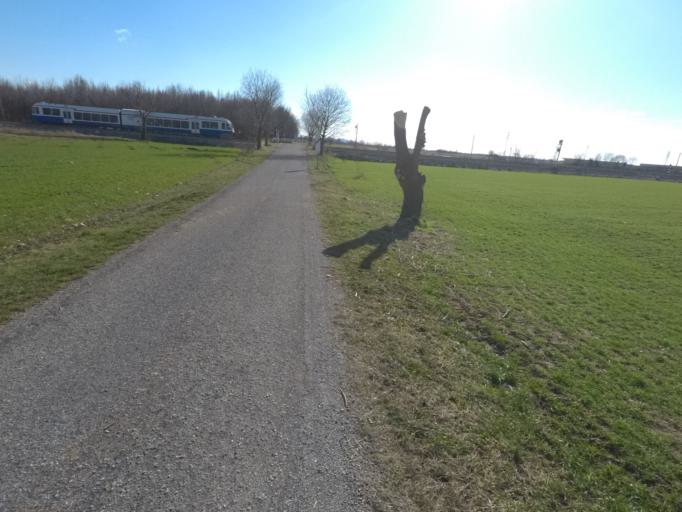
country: IT
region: Friuli Venezia Giulia
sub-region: Provincia di Udine
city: Cividale del Friuli
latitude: 46.0927
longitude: 13.4044
